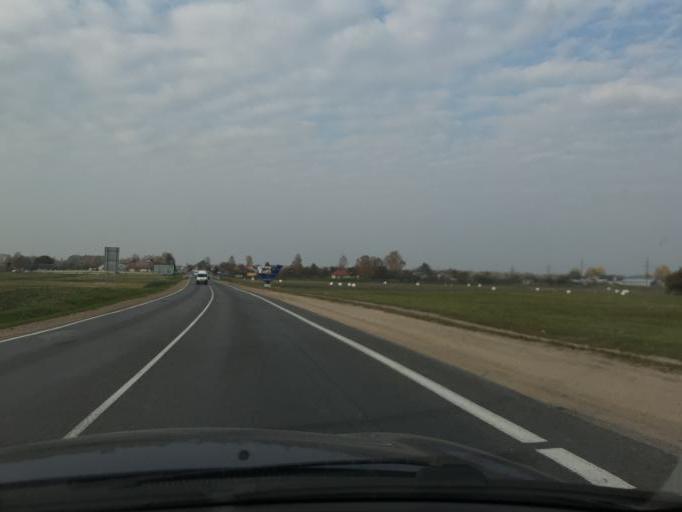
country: BY
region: Grodnenskaya
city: Lida
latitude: 53.8535
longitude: 25.3371
